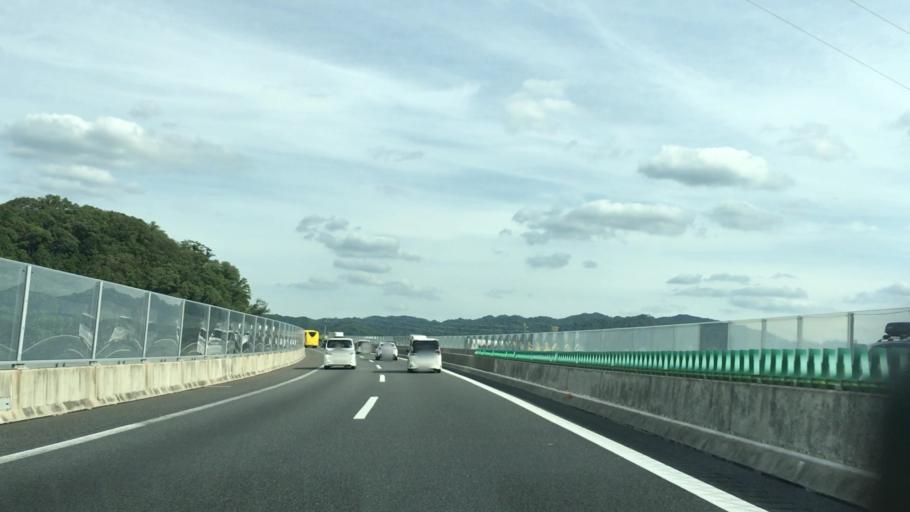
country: JP
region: Shiga Prefecture
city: Kusatsu
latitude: 34.9668
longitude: 135.9618
